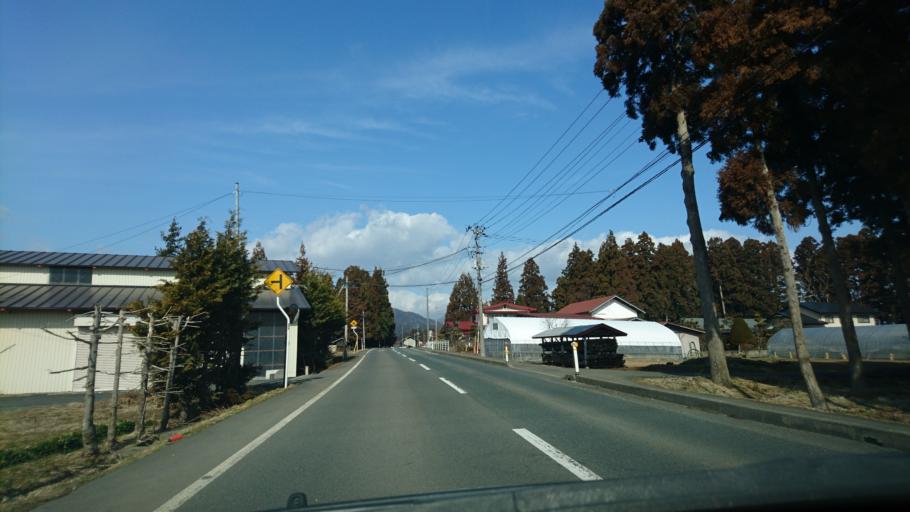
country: JP
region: Iwate
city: Hanamaki
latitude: 39.5228
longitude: 141.1242
